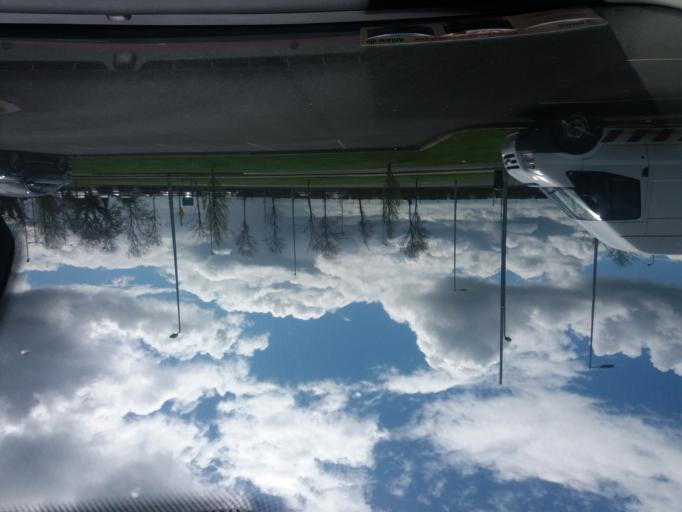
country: IE
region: Leinster
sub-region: Kildare
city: Cherryville
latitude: 53.1451
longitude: -7.0115
